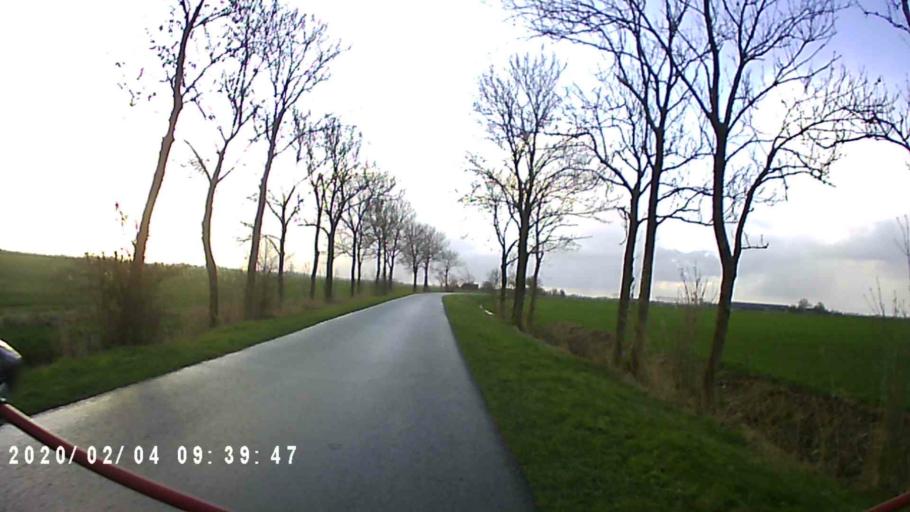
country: NL
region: Groningen
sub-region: Gemeente Zuidhorn
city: Aduard
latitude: 53.3008
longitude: 6.4690
